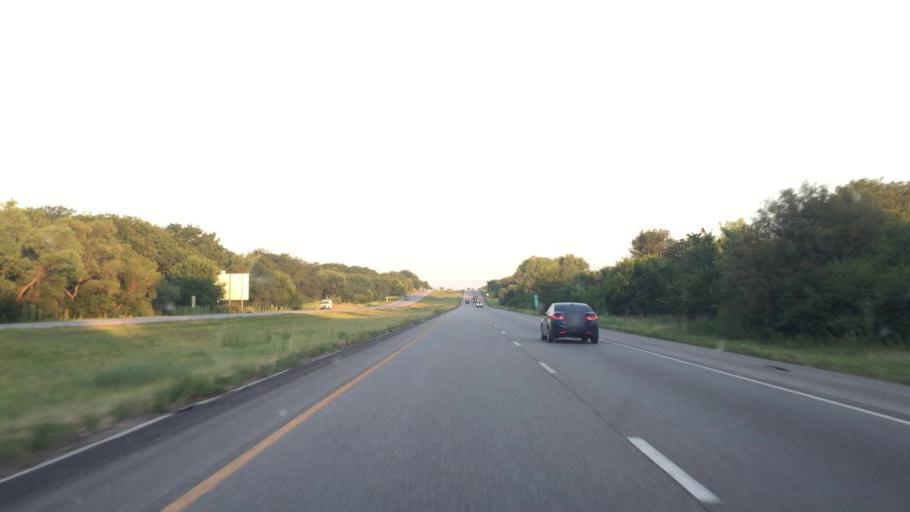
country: US
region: Missouri
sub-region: Clay County
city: Smithville
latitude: 39.3109
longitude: -94.5196
